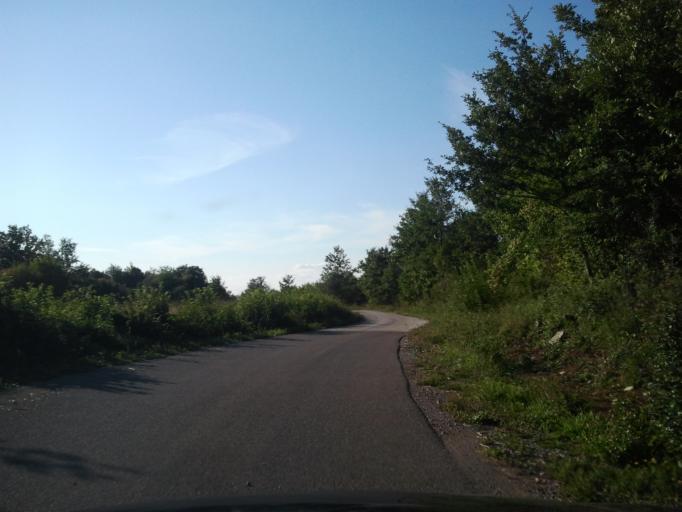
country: HR
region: Zadarska
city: Gracac
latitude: 44.3833
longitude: 15.6994
